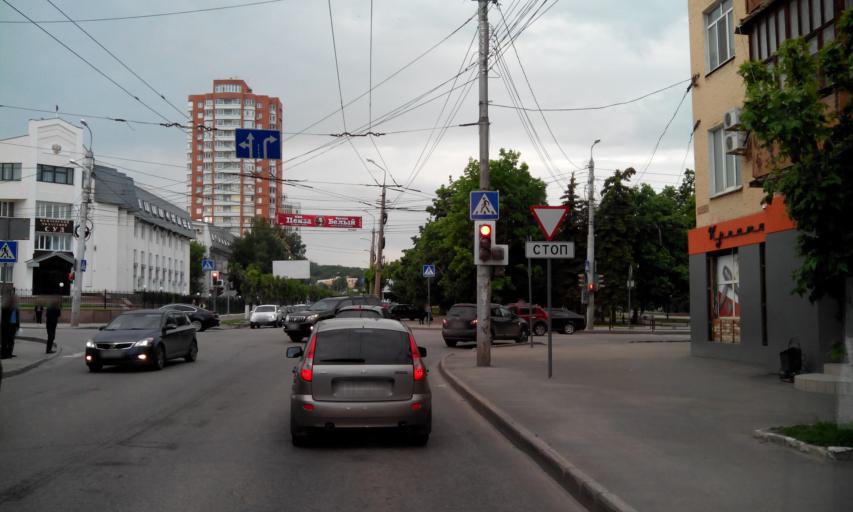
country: RU
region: Penza
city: Penza
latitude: 53.1925
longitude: 45.0143
